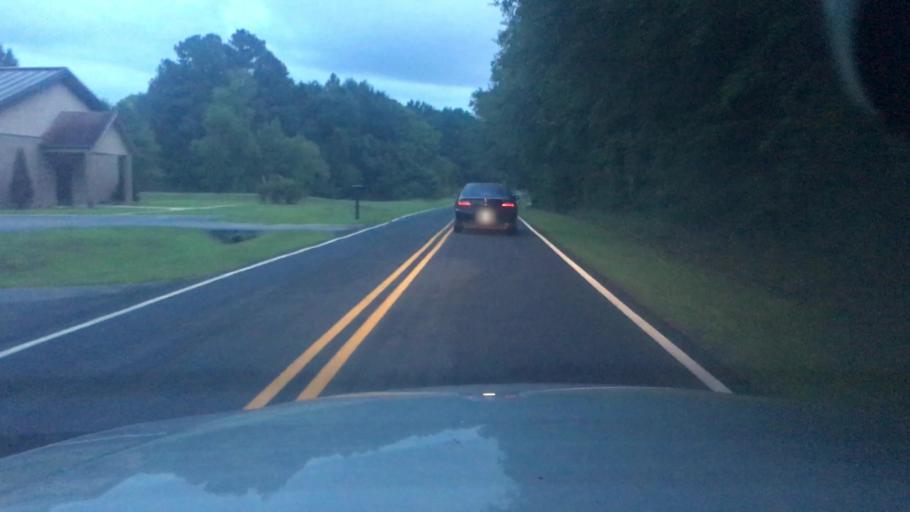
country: US
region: North Carolina
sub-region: Cumberland County
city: Hope Mills
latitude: 34.9638
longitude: -78.9259
